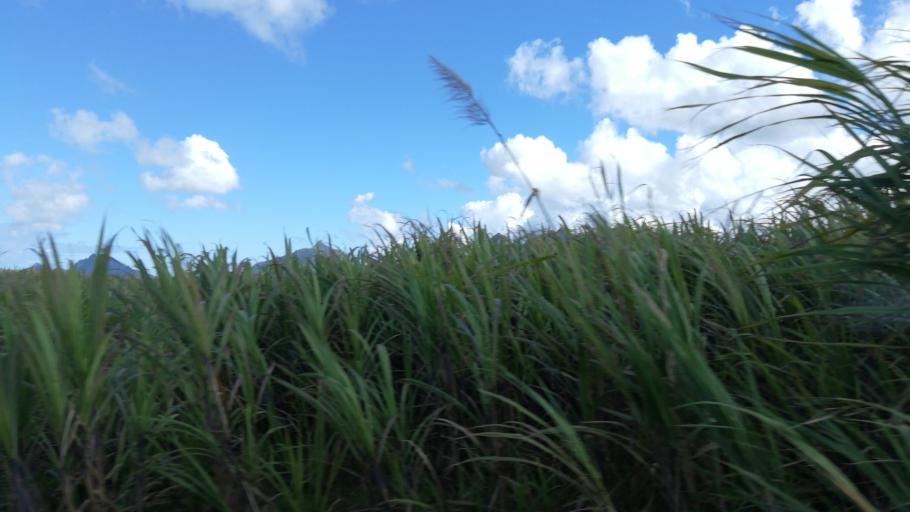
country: MU
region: Moka
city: Quartier Militaire
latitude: -20.2257
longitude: 57.5791
